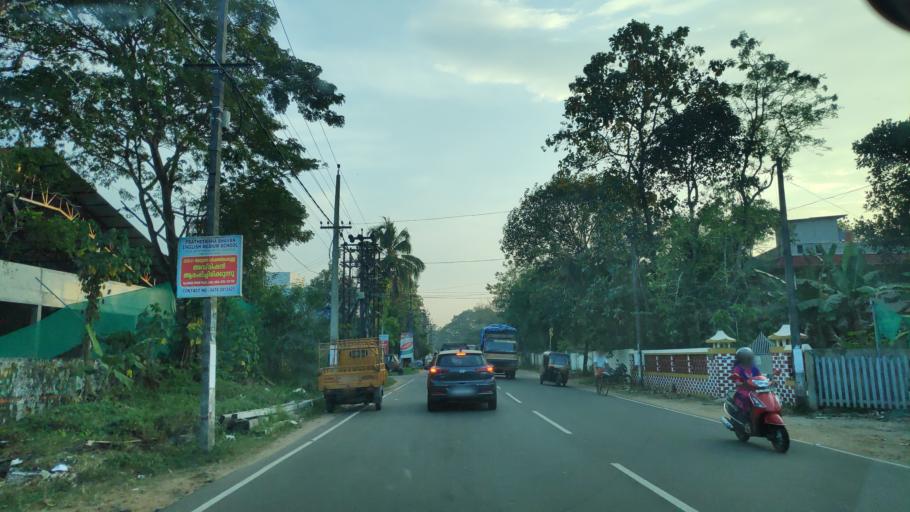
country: IN
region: Kerala
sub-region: Alappuzha
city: Shertallai
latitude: 9.6777
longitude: 76.3409
